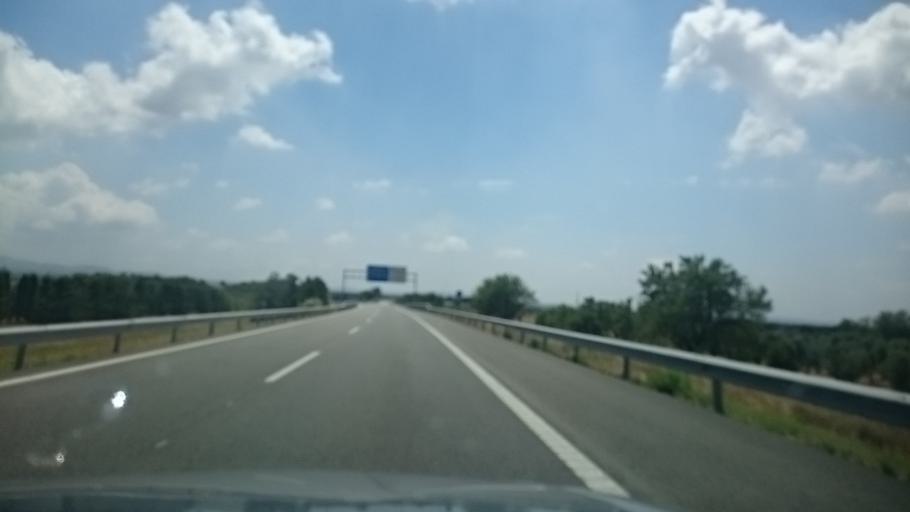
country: ES
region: Catalonia
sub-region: Provincia de Tarragona
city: El Pla de Santa Maria
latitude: 41.3719
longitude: 1.2986
